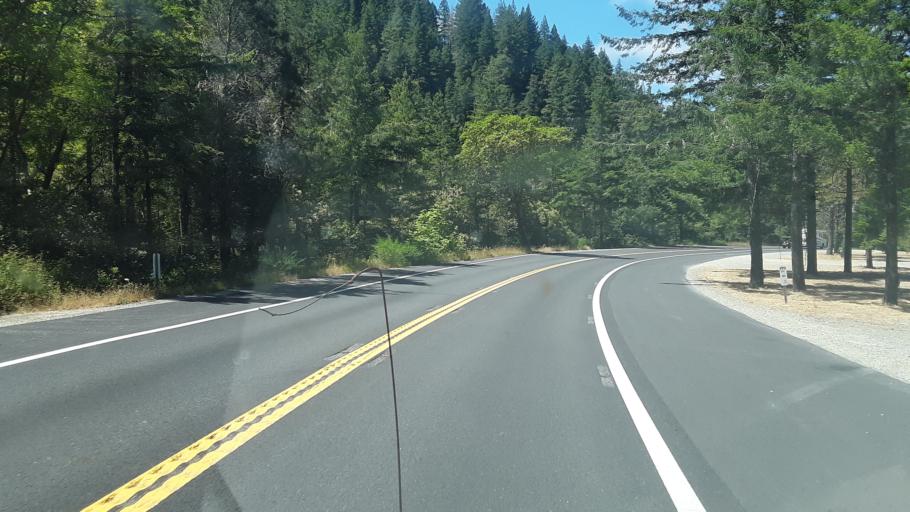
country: US
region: California
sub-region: Del Norte County
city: Bertsch-Oceanview
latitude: 41.8098
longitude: -124.0455
